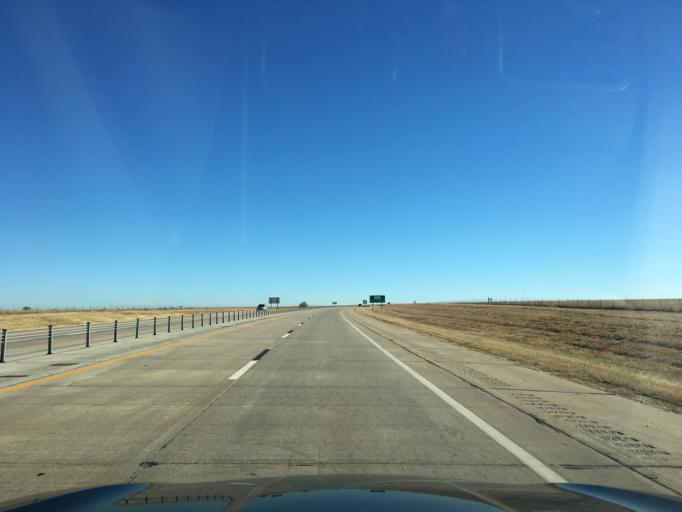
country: US
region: Oklahoma
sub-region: Noble County
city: Perry
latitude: 36.3826
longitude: -97.0570
